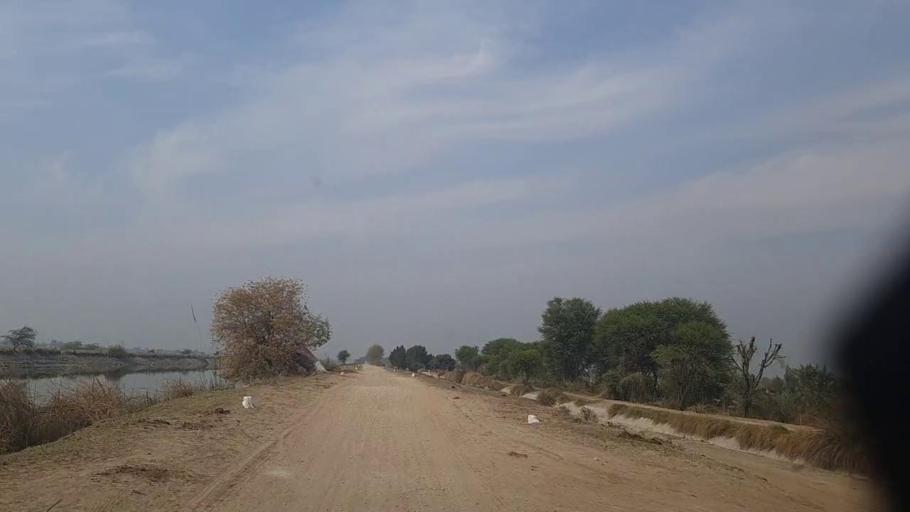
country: PK
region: Sindh
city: Daur
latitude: 26.3277
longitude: 68.1927
